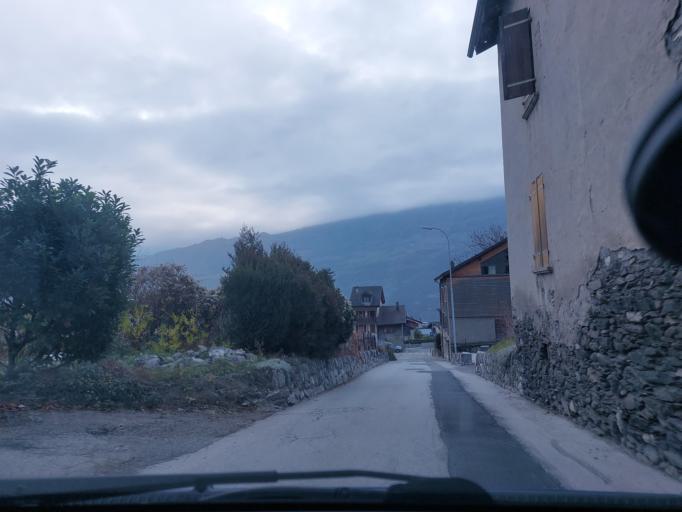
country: CH
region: Valais
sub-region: Conthey District
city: Chamoson
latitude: 46.2031
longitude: 7.2224
